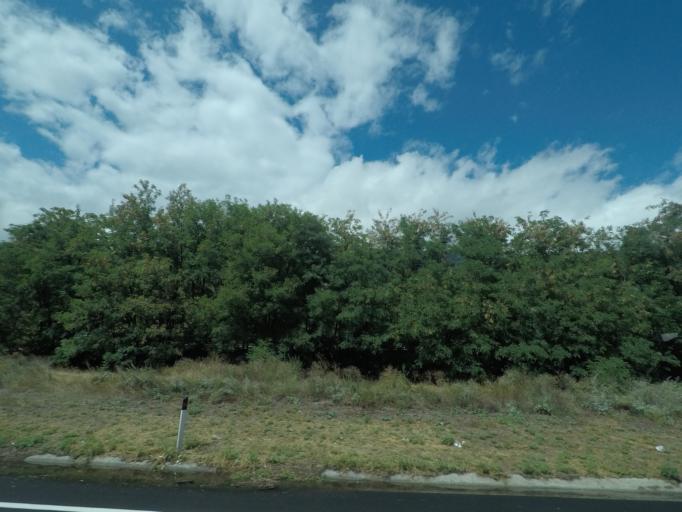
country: IT
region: Aosta Valley
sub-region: Valle d'Aosta
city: Villefranche
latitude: 45.7396
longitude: 7.4276
